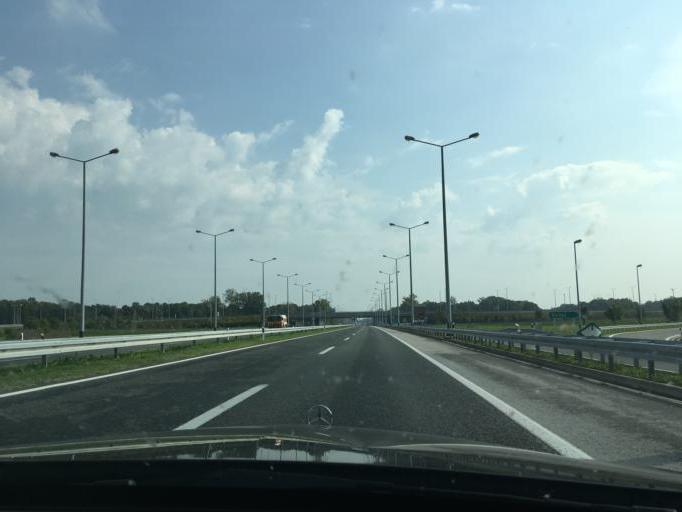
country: HR
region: Brodsko-Posavska
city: Vrpolje
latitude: 45.1448
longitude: 18.3065
